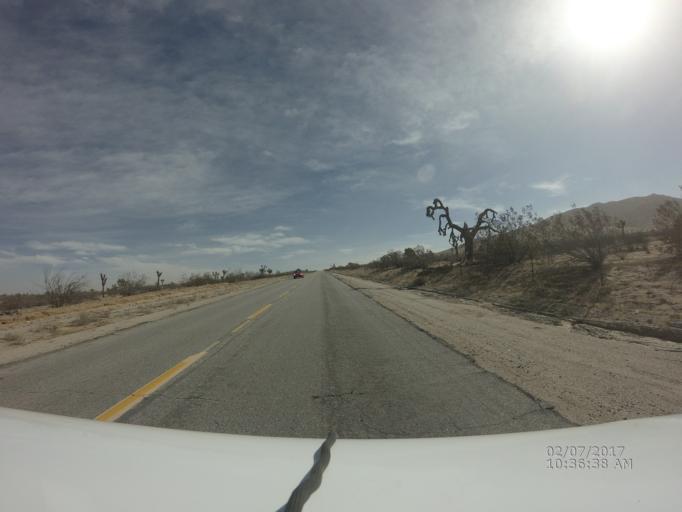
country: US
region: California
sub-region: Los Angeles County
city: Lake Los Angeles
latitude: 34.6901
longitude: -117.8079
